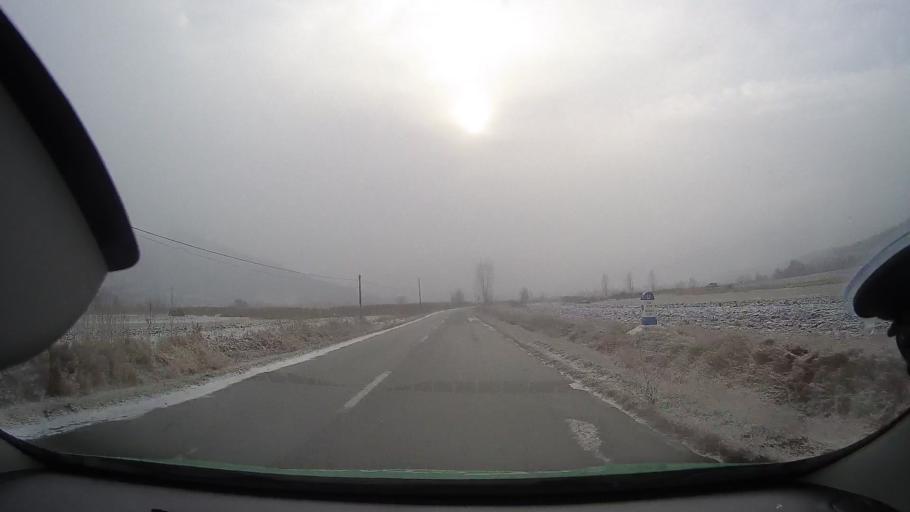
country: RO
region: Alba
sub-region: Comuna Rimetea
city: Rimetea
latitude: 46.4116
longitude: 23.5588
